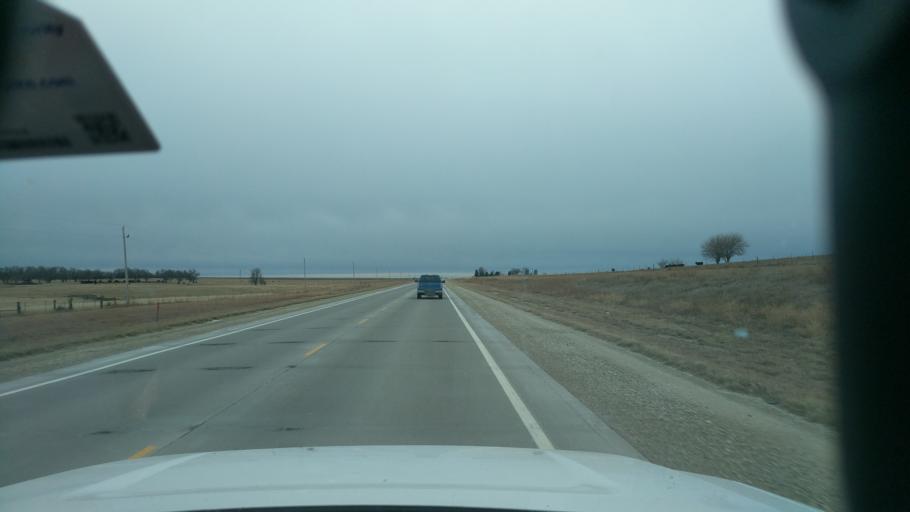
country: US
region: Kansas
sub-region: Dickinson County
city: Herington
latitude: 38.6063
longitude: -96.9486
